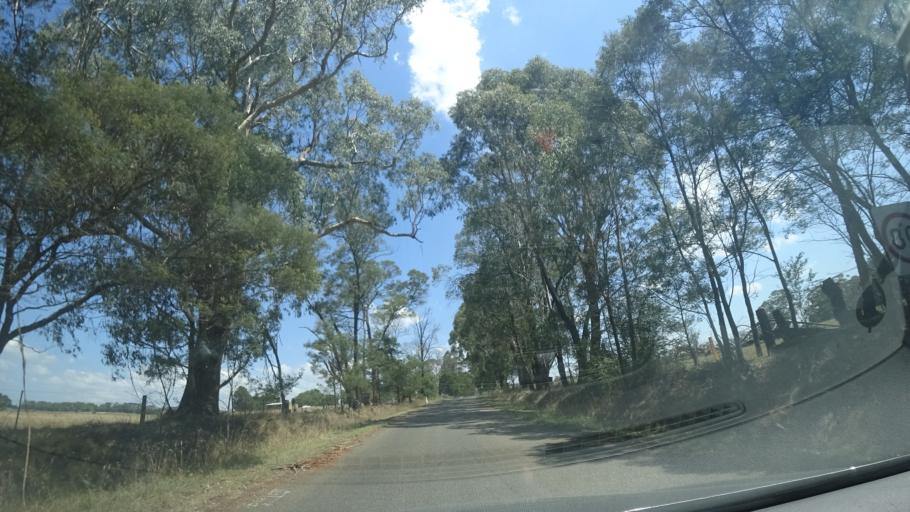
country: AU
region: New South Wales
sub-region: Wingecarribee
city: Bundanoon
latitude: -34.6094
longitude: 150.2804
